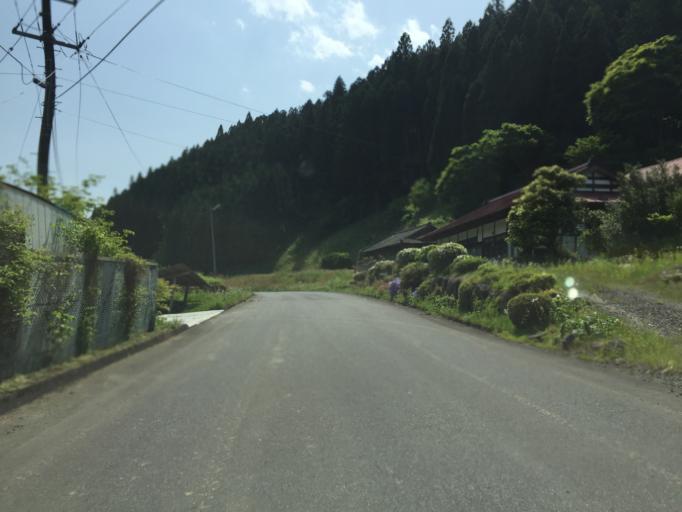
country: JP
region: Fukushima
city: Ishikawa
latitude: 37.0513
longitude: 140.5785
